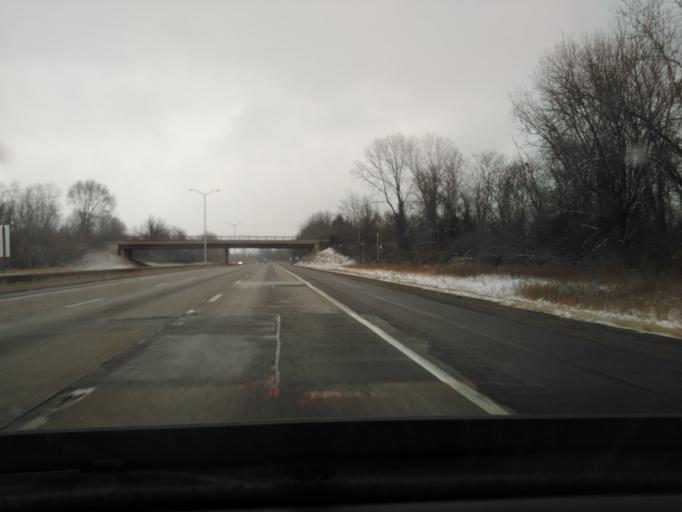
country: US
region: Illinois
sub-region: Saint Clair County
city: Alorton
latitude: 38.5870
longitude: -90.1000
